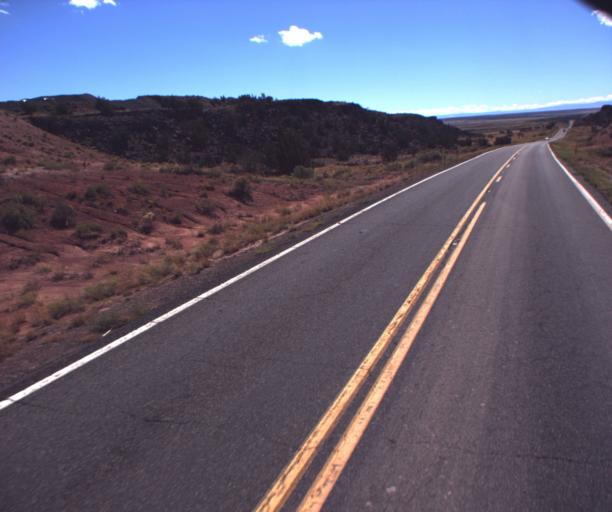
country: US
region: Arizona
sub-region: Apache County
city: Saint Johns
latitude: 34.7562
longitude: -109.2435
